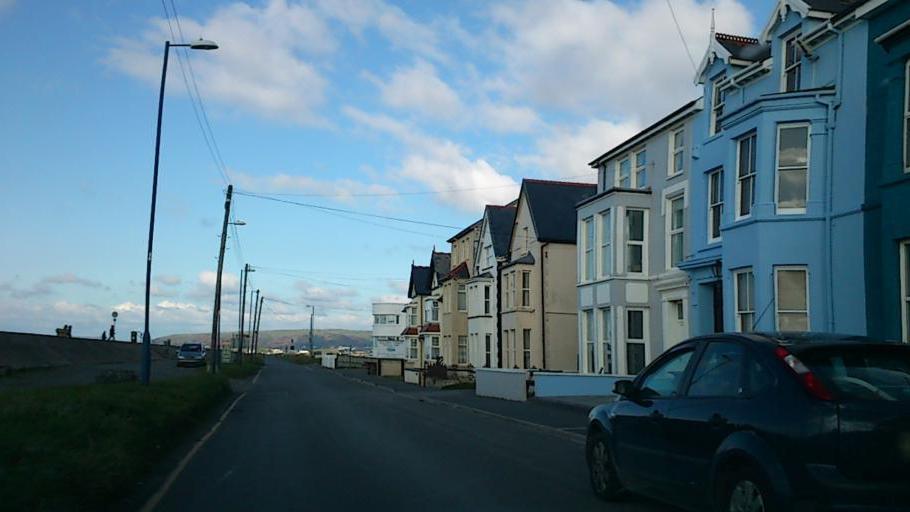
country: GB
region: Wales
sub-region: County of Ceredigion
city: Bow Street
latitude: 52.4957
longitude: -4.0519
